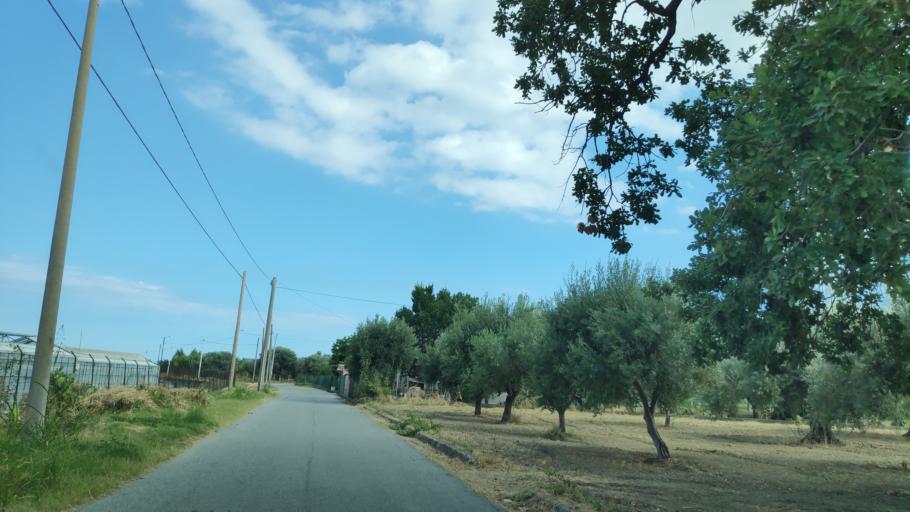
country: IT
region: Calabria
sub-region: Provincia di Catanzaro
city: Guardavalle Marina
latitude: 38.4656
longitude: 16.5706
